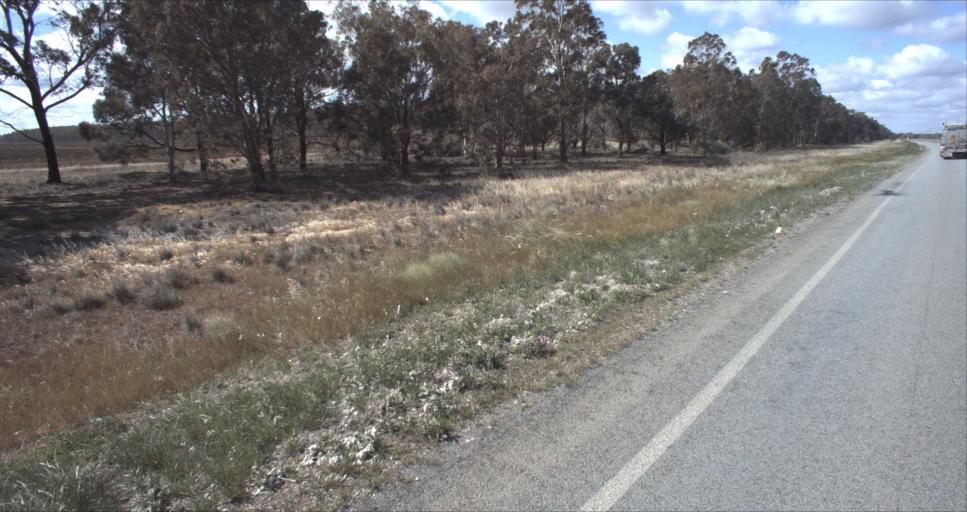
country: AU
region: New South Wales
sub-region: Murrumbidgee Shire
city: Darlington Point
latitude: -34.5789
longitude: 146.1655
